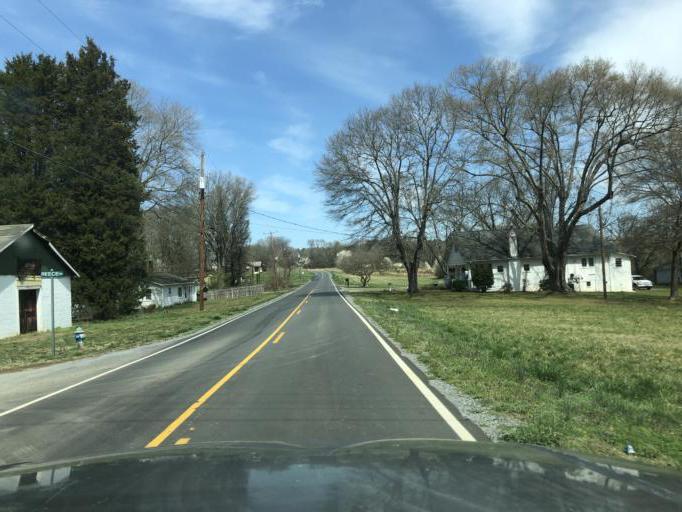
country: US
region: North Carolina
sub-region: Cleveland County
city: Shelby
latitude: 35.2609
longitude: -81.5431
